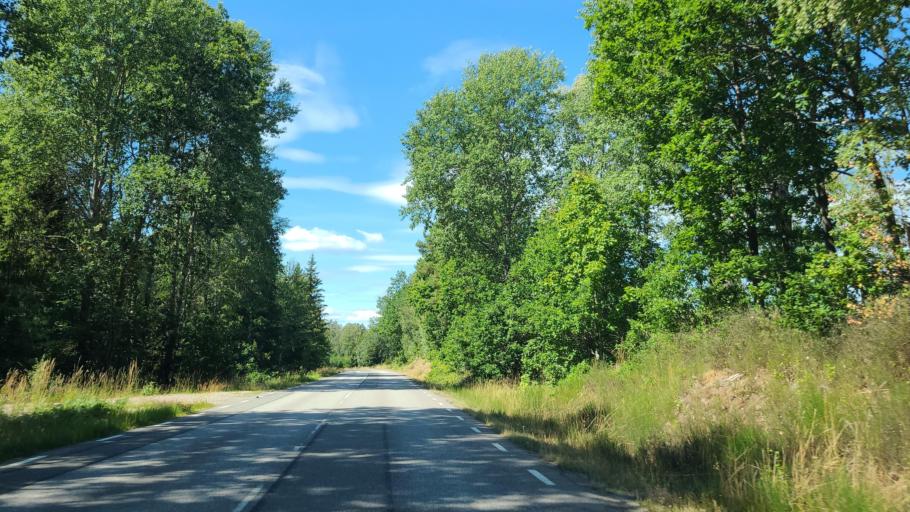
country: SE
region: Kalmar
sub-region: Emmaboda Kommun
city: Emmaboda
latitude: 56.5559
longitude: 15.7266
